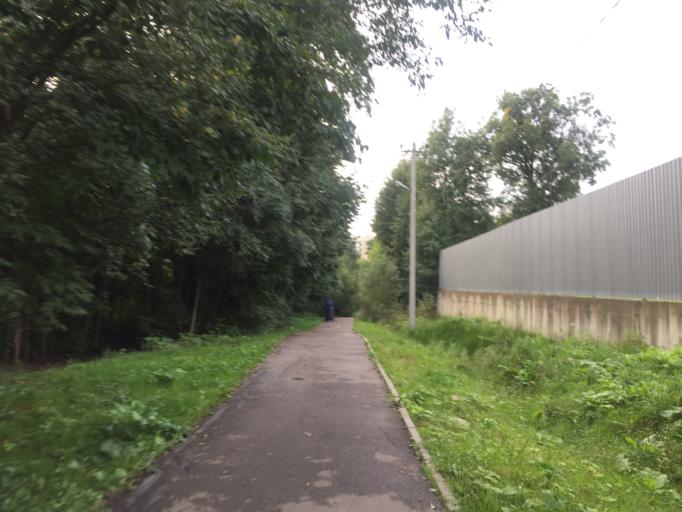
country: RU
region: Leningrad
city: Murino
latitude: 60.0427
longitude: 30.4701
